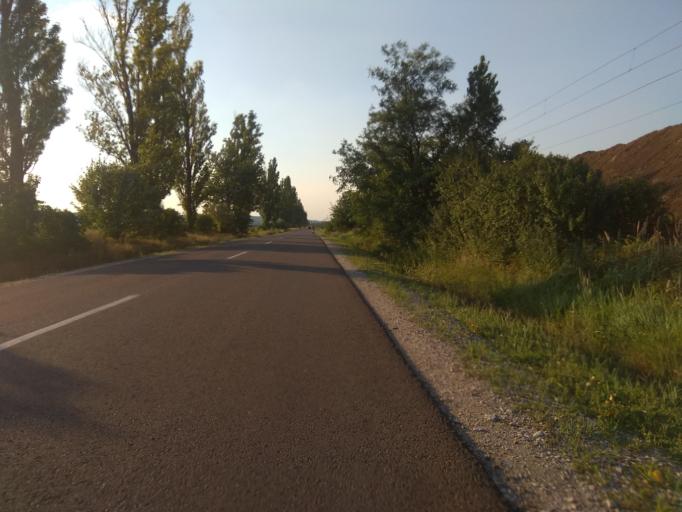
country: HU
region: Borsod-Abauj-Zemplen
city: Nyekladhaza
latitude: 47.9773
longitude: 20.8474
